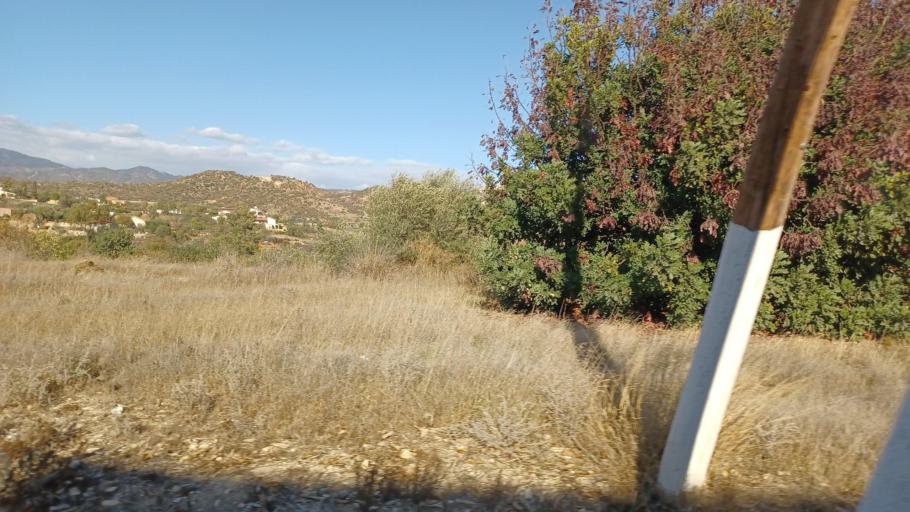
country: CY
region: Limassol
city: Pyrgos
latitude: 34.7771
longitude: 33.2507
